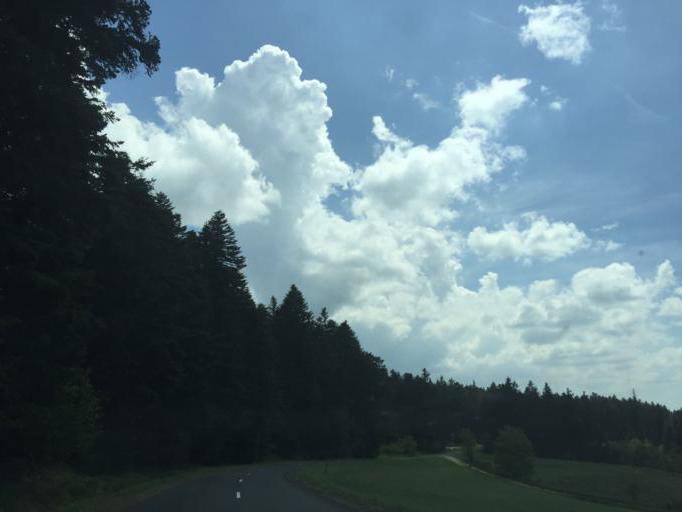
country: FR
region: Rhone-Alpes
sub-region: Departement de la Loire
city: Saint-Sauveur-en-Rue
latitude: 45.3094
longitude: 4.4637
